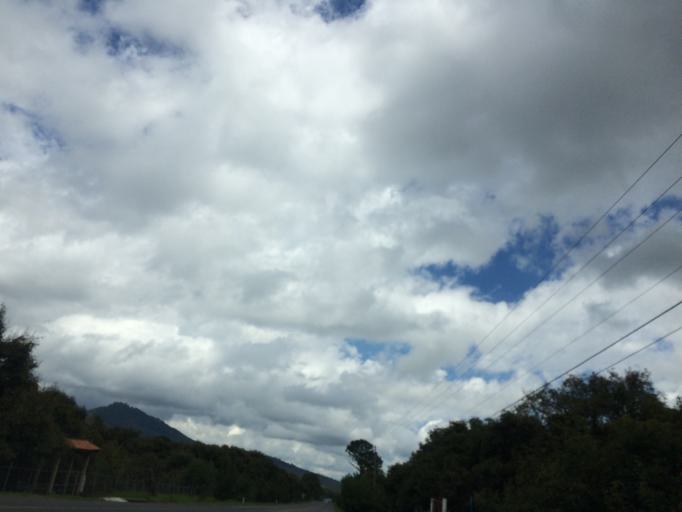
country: MX
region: Michoacan
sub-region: Uruapan
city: Santa Ana Zirosto
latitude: 19.5476
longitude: -102.3145
